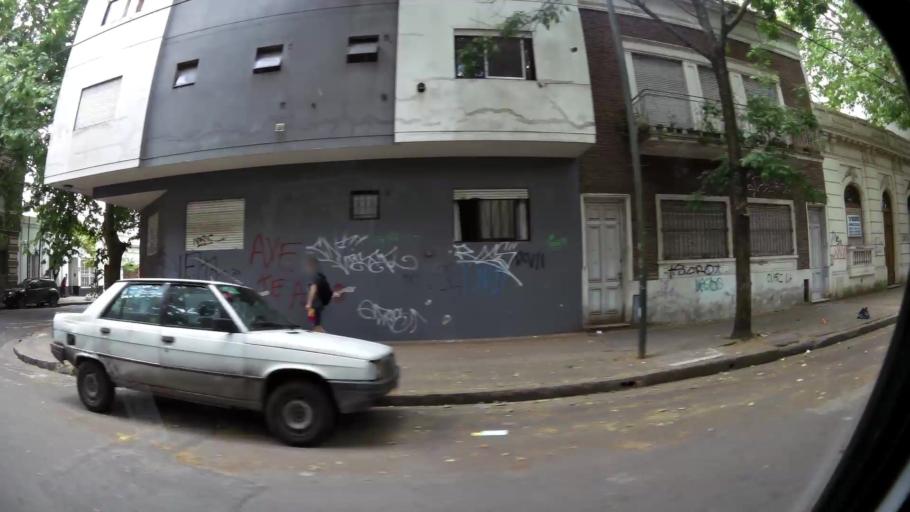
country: AR
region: Buenos Aires
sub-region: Partido de La Plata
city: La Plata
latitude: -34.9137
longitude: -57.9395
